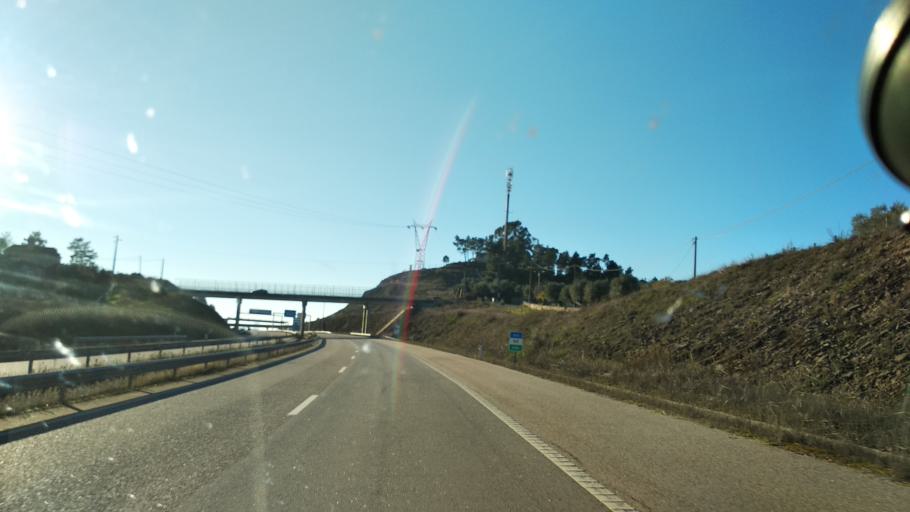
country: PT
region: Santarem
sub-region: Abrantes
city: Alferrarede
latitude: 39.4963
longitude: -8.0889
